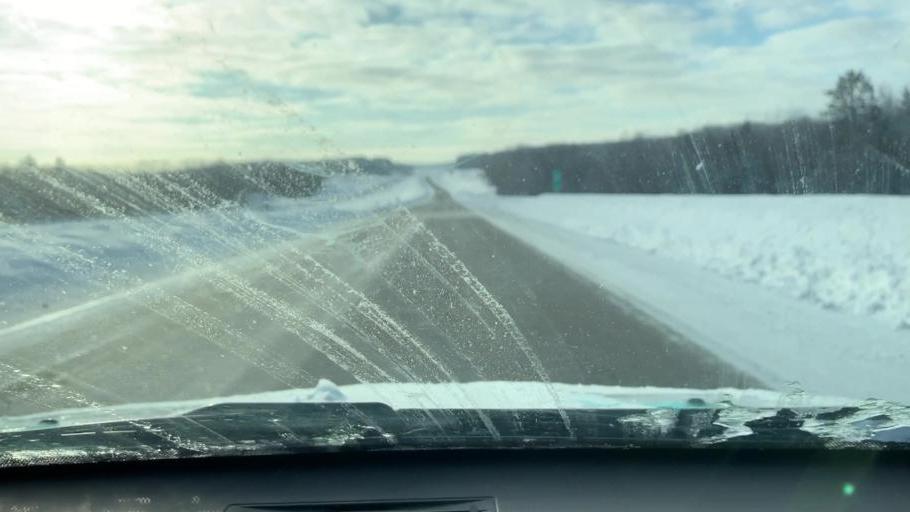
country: US
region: Michigan
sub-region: Wexford County
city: Cadillac
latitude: 44.3306
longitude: -85.4055
